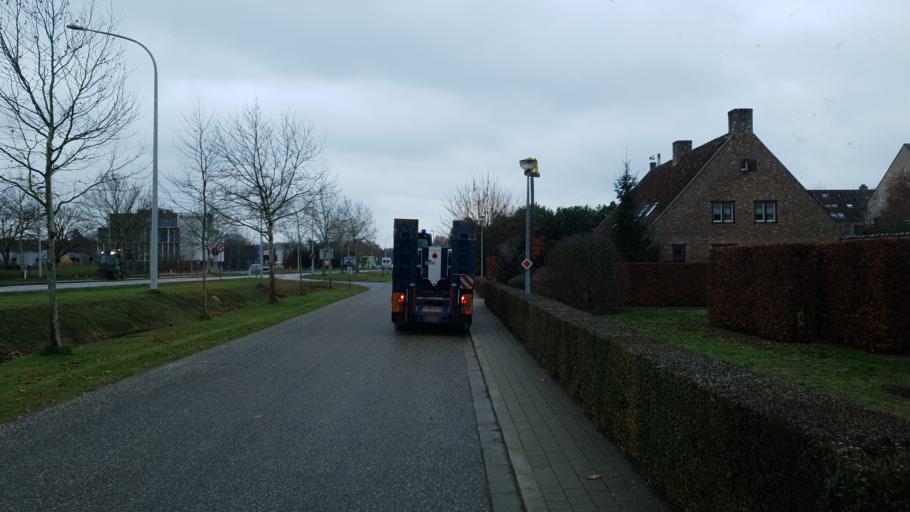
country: BE
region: Flanders
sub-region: Provincie Antwerpen
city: Herentals
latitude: 51.1786
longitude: 4.8500
